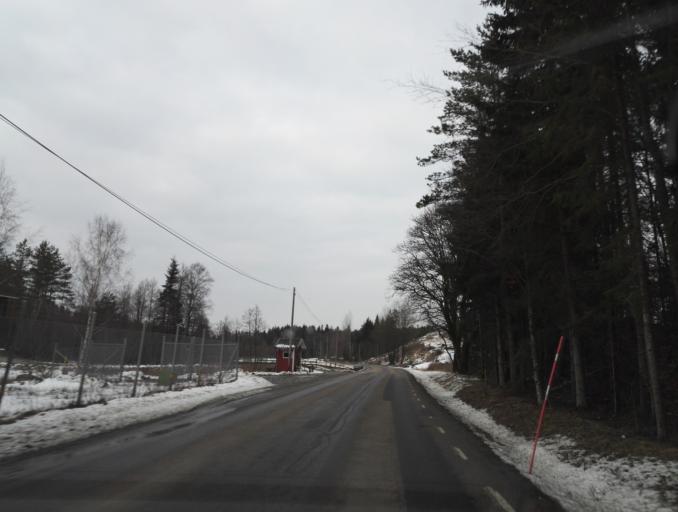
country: SE
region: Vaestra Goetaland
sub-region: Bollebygds Kommun
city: Bollebygd
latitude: 57.7345
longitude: 12.5919
